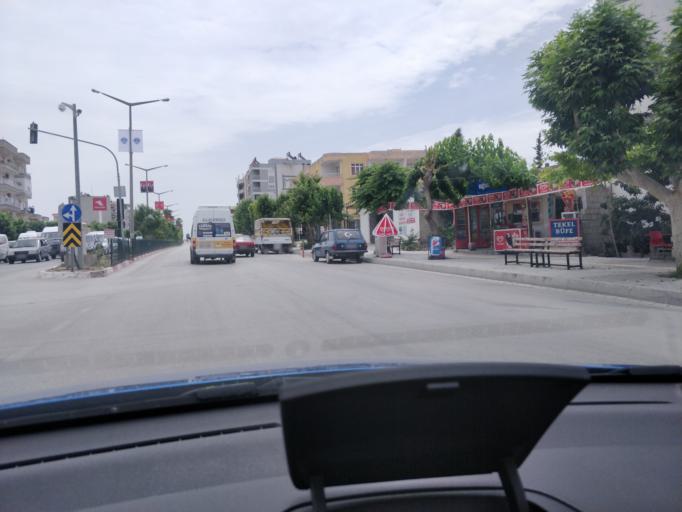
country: TR
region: Mersin
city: Mut
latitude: 36.6420
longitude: 33.4406
